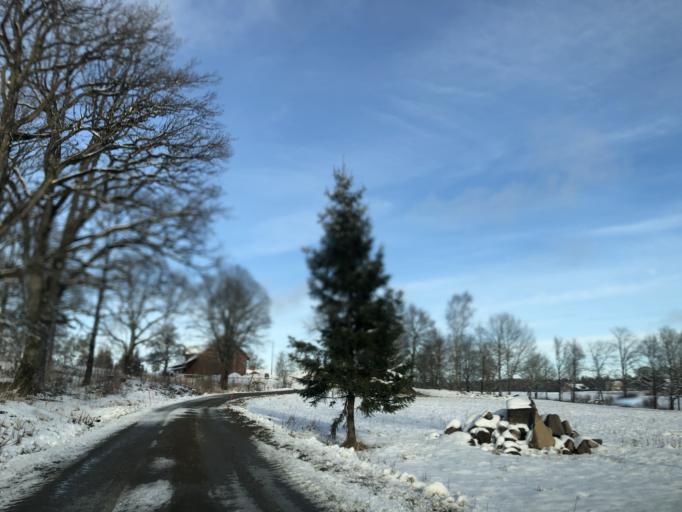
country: SE
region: Vaestra Goetaland
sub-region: Ulricehamns Kommun
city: Ulricehamn
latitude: 57.7337
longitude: 13.4846
